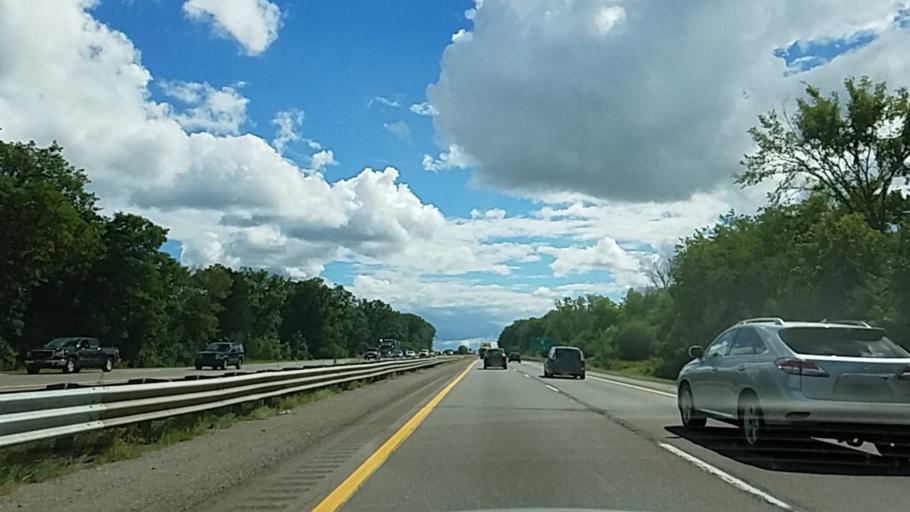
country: US
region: Michigan
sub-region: Washtenaw County
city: Ann Arbor
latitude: 42.3297
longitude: -83.7430
